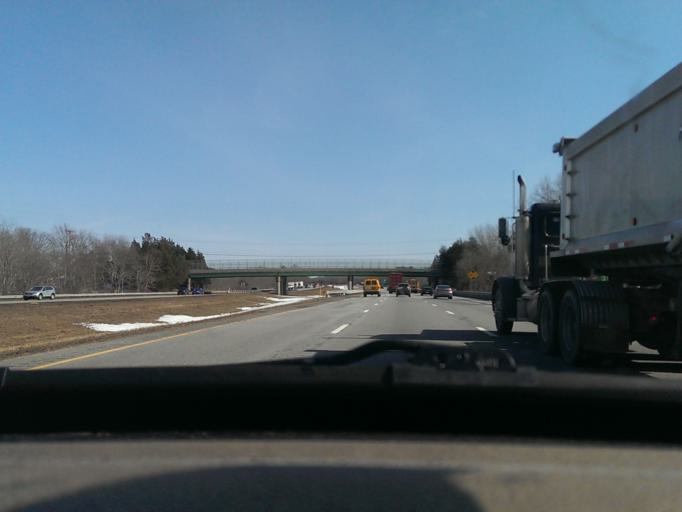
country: US
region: Rhode Island
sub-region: Bristol County
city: Barrington
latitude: 41.7827
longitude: -71.2901
